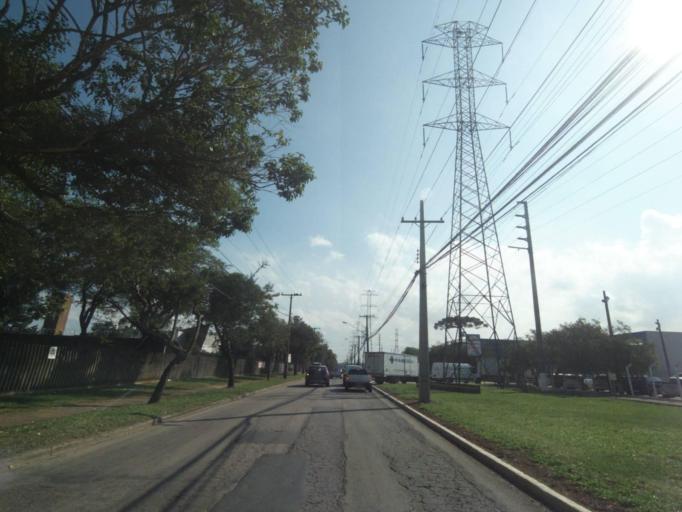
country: BR
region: Parana
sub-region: Araucaria
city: Araucaria
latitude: -25.5308
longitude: -49.3283
